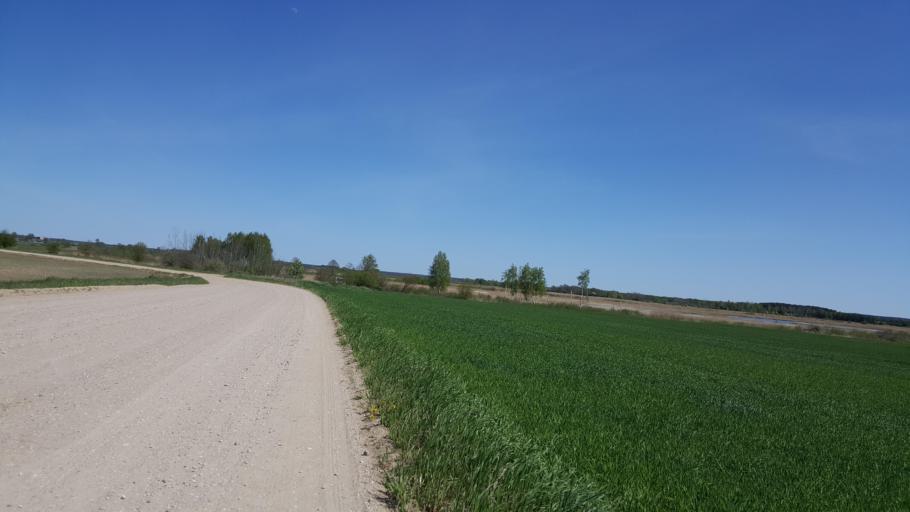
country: BY
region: Brest
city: Kamyanyets
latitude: 52.4462
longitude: 23.8622
